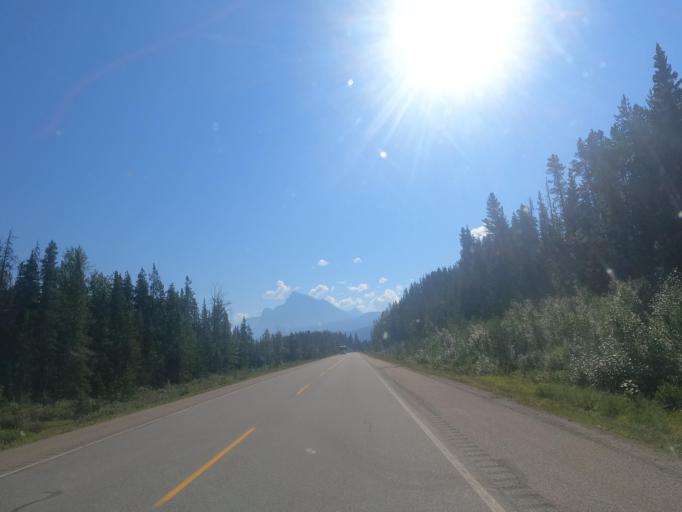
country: CA
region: Alberta
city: Jasper Park Lodge
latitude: 52.8581
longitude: -118.6322
